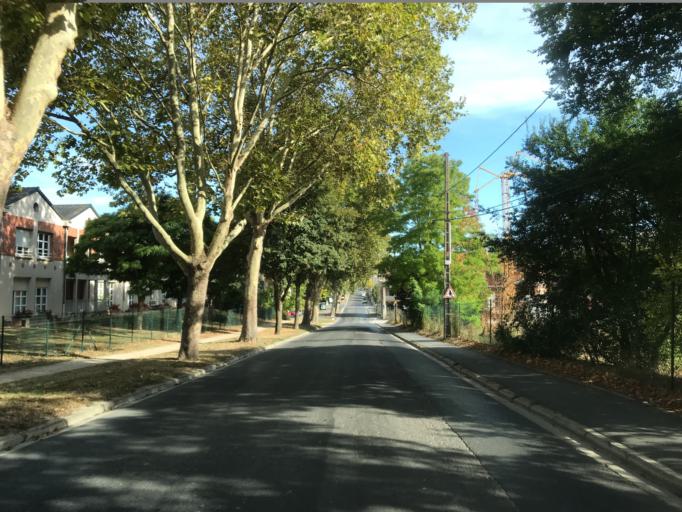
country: FR
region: Champagne-Ardenne
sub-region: Departement de la Marne
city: Pierry
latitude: 49.0292
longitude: 3.9559
